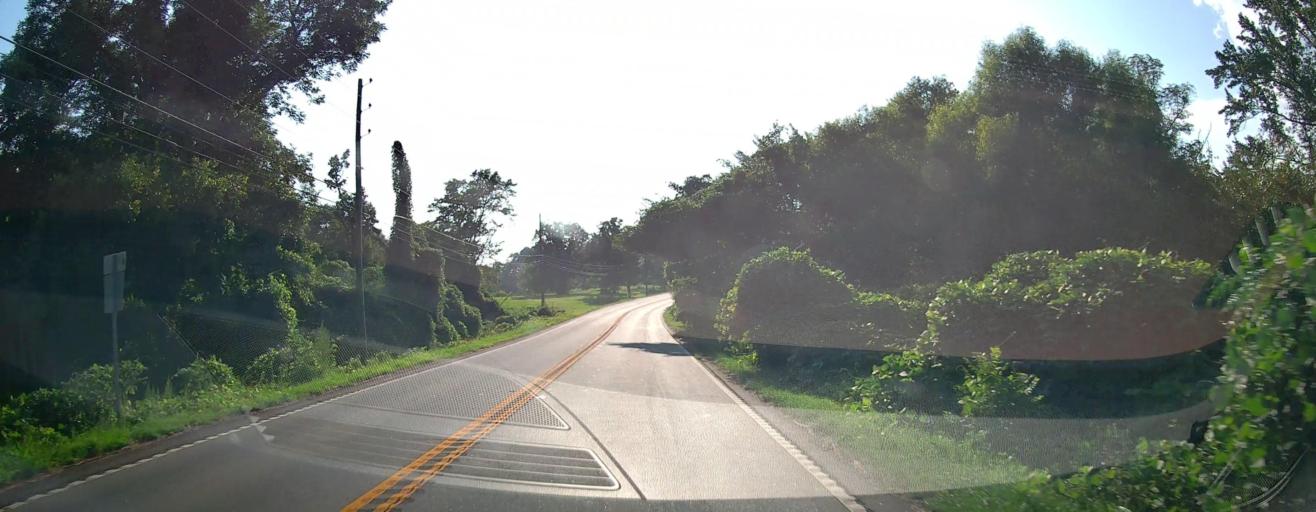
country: US
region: Georgia
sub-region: Houston County
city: Perry
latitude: 32.5029
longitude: -83.6341
